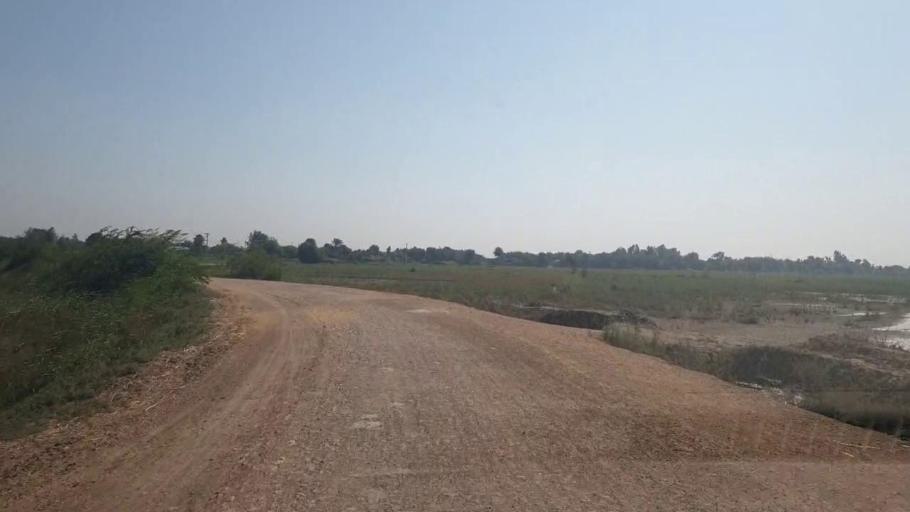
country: PK
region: Sindh
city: Badin
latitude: 24.6805
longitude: 68.8652
